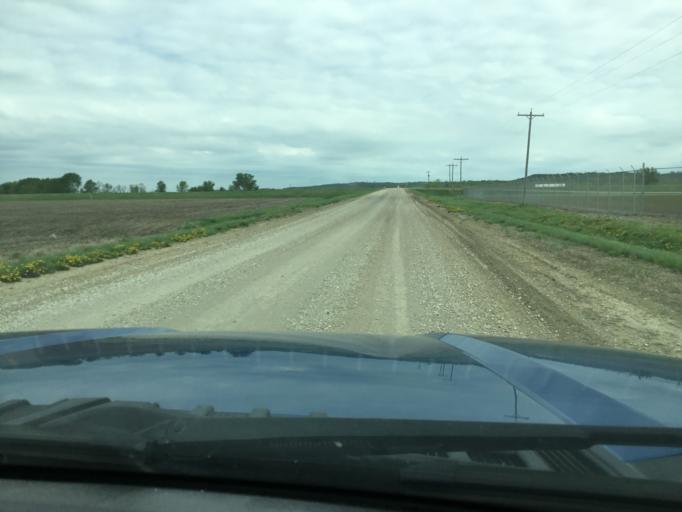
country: US
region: Kansas
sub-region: Douglas County
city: Lawrence
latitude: 39.0205
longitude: -95.2242
